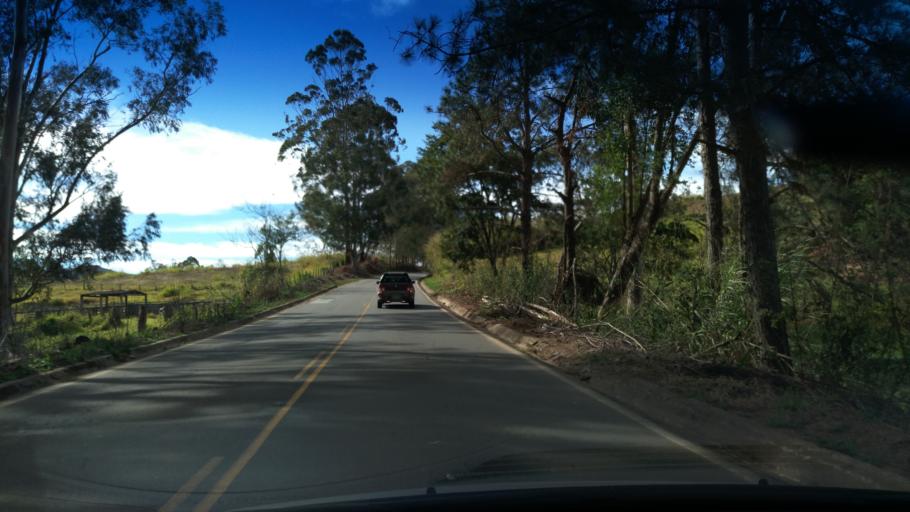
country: BR
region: Minas Gerais
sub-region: Andradas
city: Andradas
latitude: -22.0661
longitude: -46.4643
